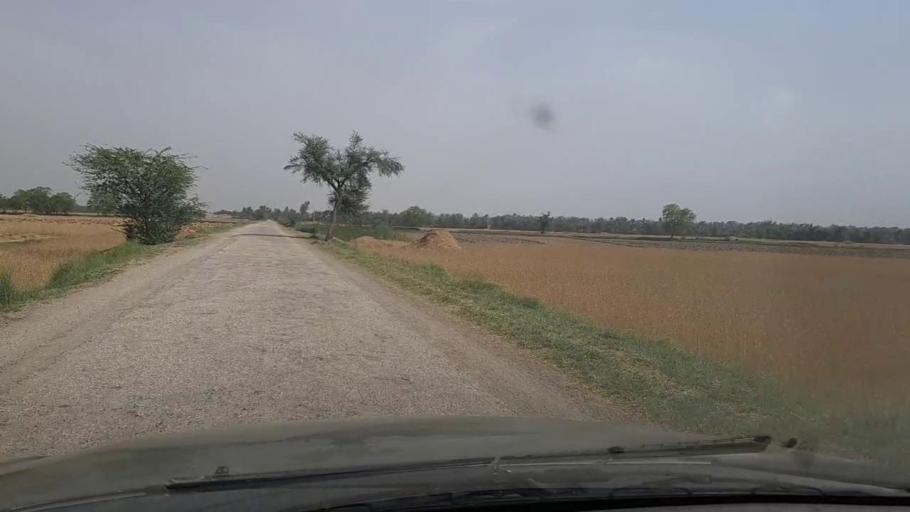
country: PK
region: Sindh
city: Lakhi
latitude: 27.8469
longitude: 68.7560
